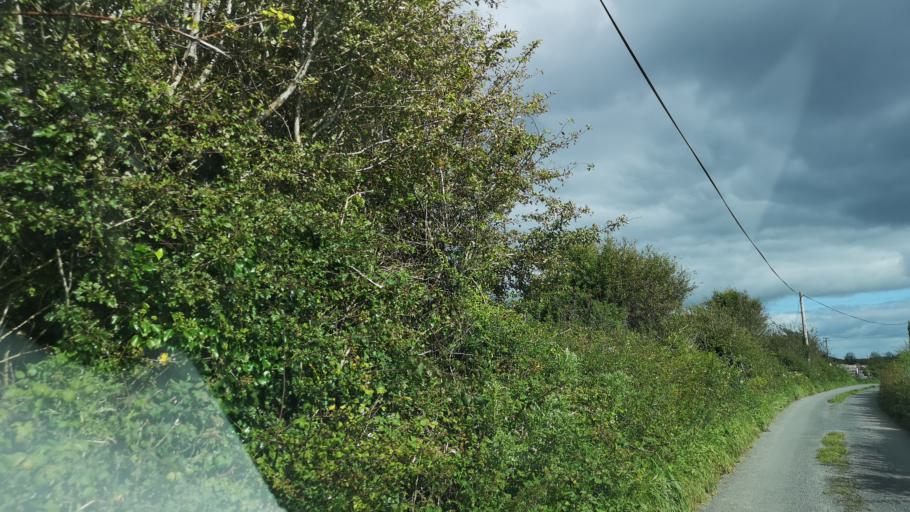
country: IE
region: Connaught
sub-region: County Galway
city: Moycullen
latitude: 53.3195
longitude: -9.1404
